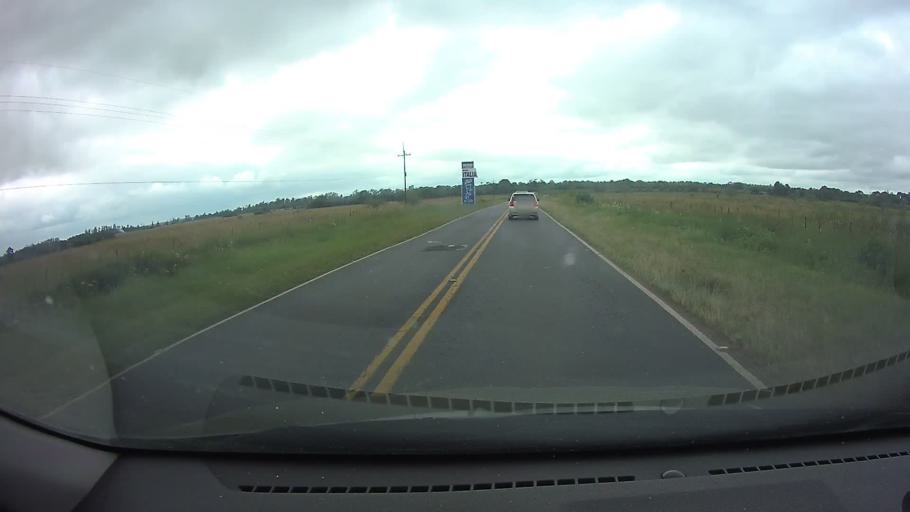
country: PY
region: Central
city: Nueva Italia
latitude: -25.5602
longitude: -57.5012
